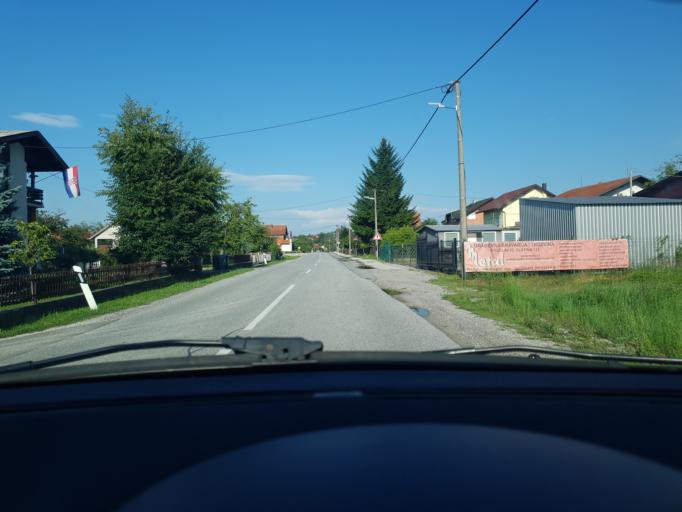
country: HR
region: Zagrebacka
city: Jakovlje
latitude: 45.9767
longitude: 15.8755
